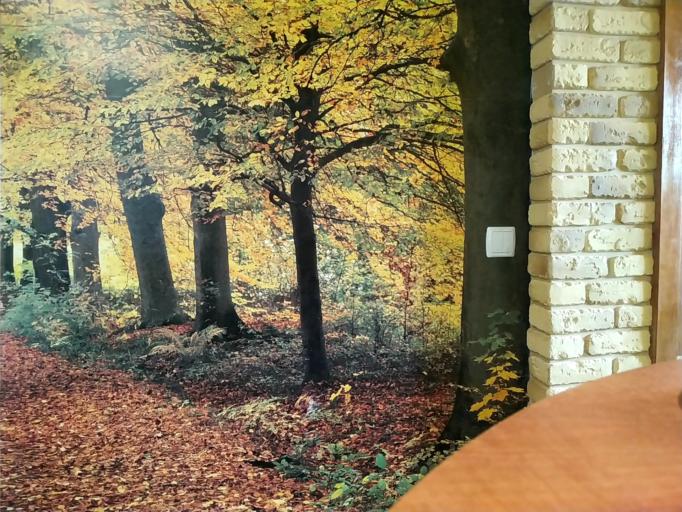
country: RU
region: Novgorod
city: Opechenskiy Posad
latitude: 58.2697
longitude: 34.0135
